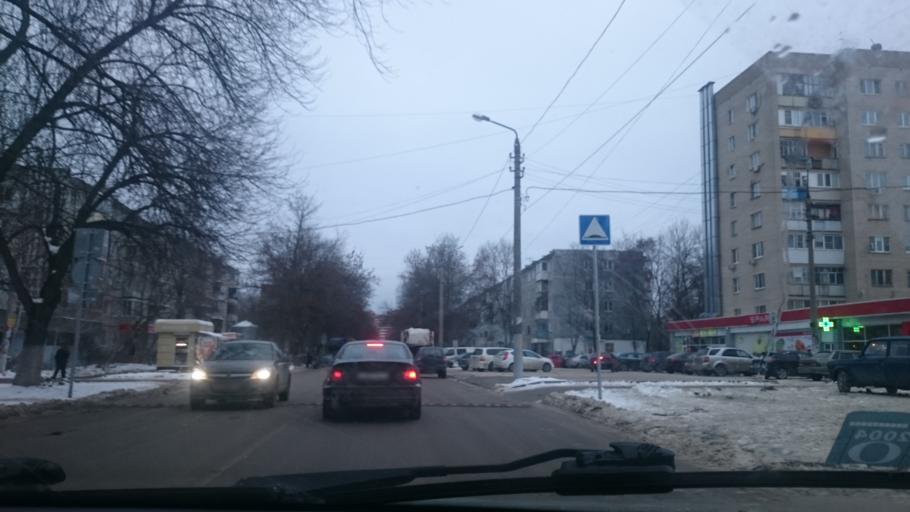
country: RU
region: Tula
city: Tula
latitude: 54.1789
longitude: 37.6339
